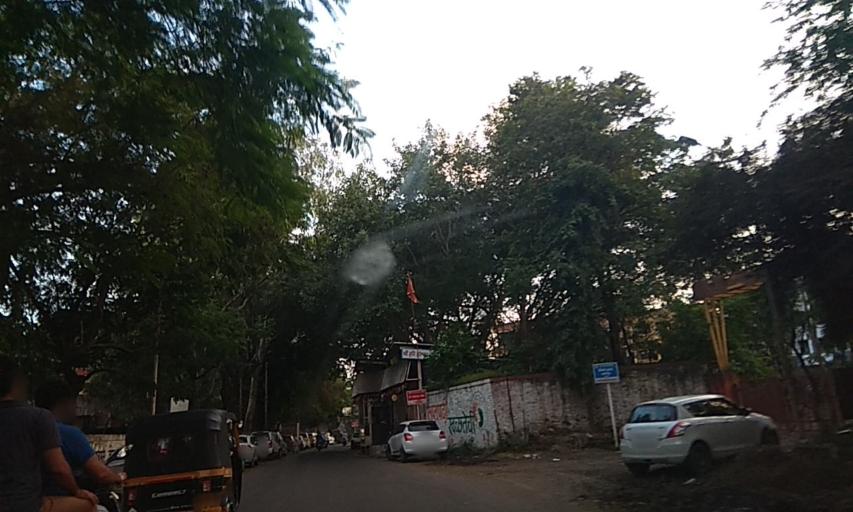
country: IN
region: Maharashtra
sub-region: Pune Division
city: Pune
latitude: 18.4960
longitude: 73.8510
